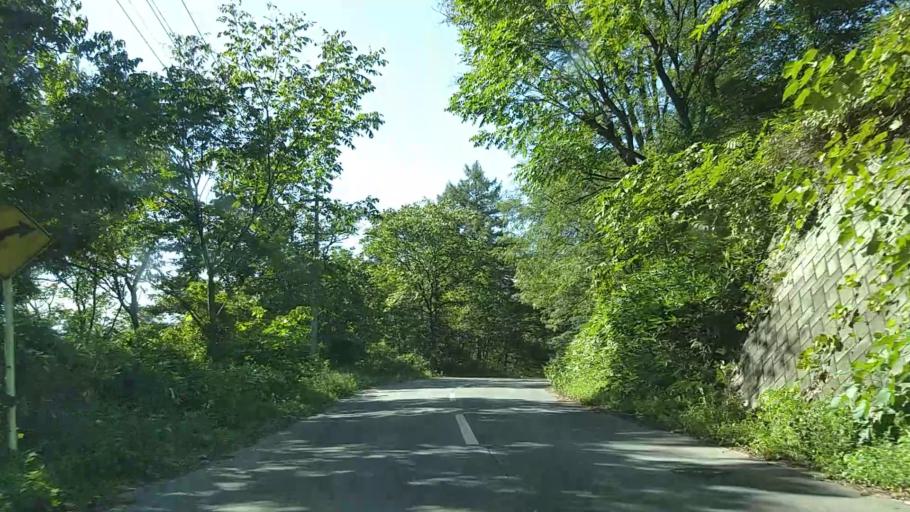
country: JP
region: Nagano
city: Nagano-shi
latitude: 36.6067
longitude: 138.0916
